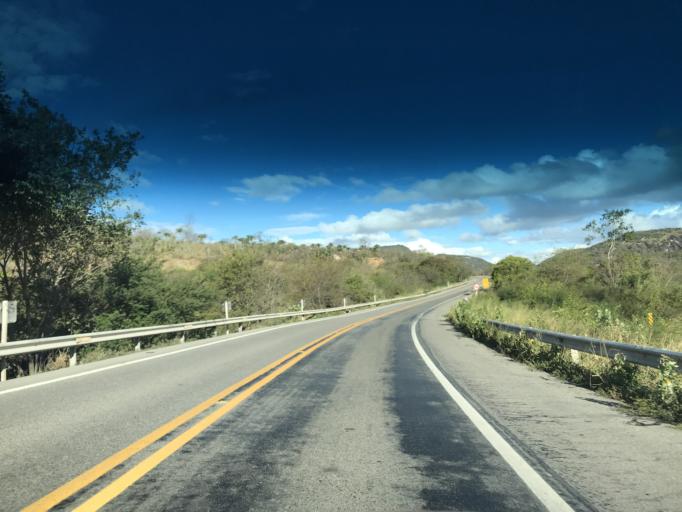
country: BR
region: Bahia
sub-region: Itaberaba
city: Itaberaba
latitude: -12.5088
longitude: -40.4457
